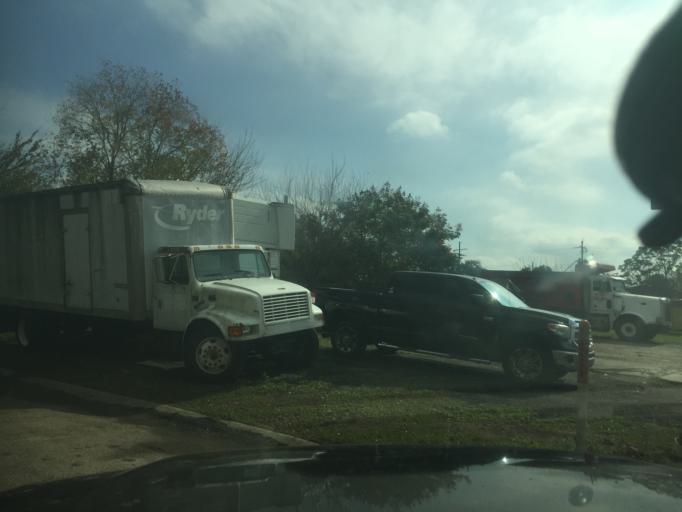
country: US
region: Louisiana
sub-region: Saint Bernard Parish
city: Arabi
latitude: 29.9992
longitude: -90.0359
